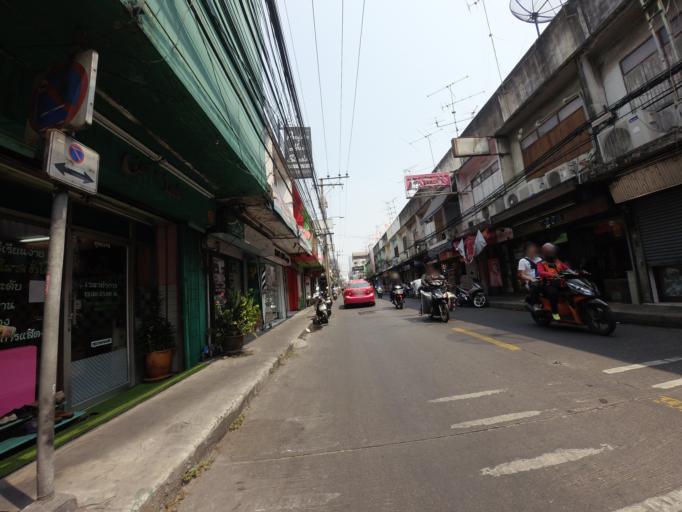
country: TH
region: Bangkok
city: Din Daeng
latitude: 13.7620
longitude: 100.5564
